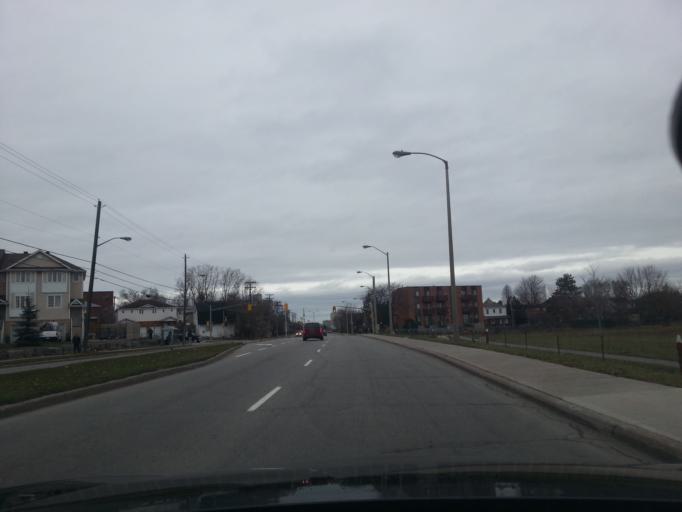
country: CA
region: Ontario
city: Ottawa
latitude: 45.3724
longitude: -75.7324
